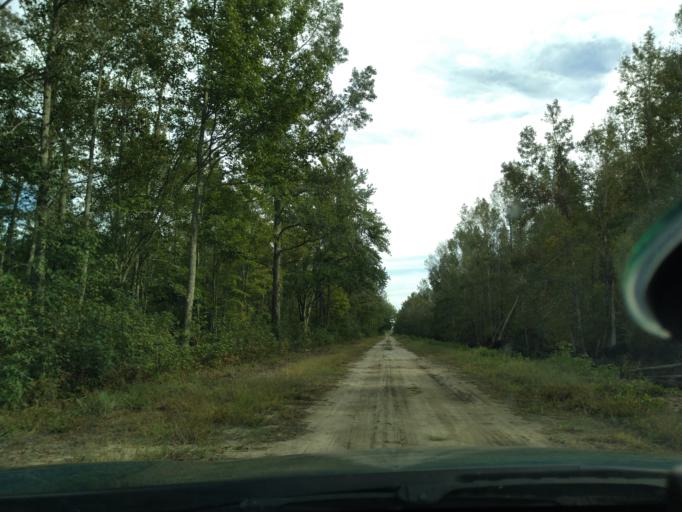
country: US
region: North Carolina
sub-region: Beaufort County
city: Belhaven
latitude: 35.6976
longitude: -76.5610
